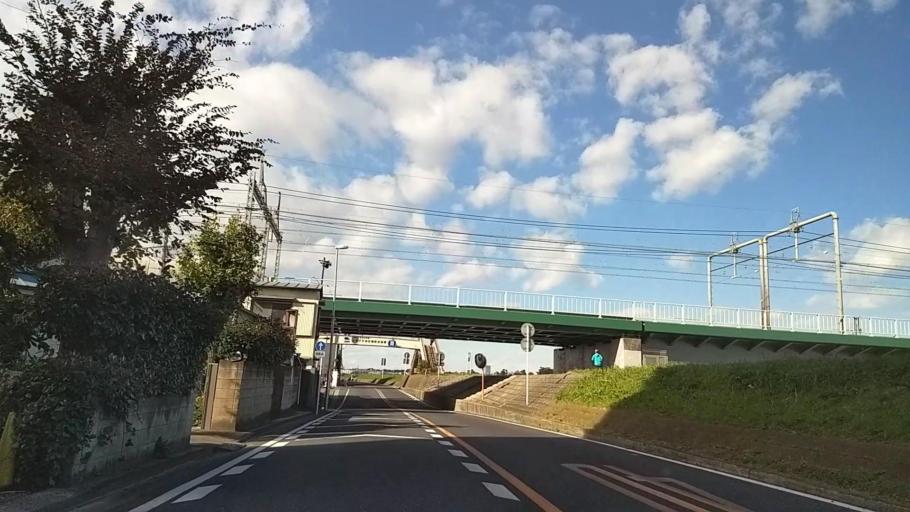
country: JP
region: Kanagawa
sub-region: Kawasaki-shi
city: Kawasaki
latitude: 35.5846
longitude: 139.6651
